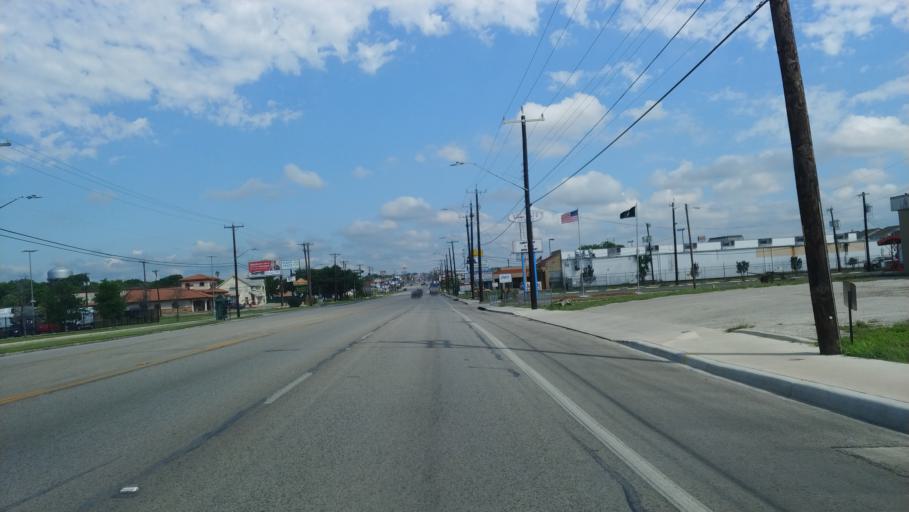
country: US
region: Texas
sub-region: Bexar County
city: Balcones Heights
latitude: 29.4761
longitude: -98.5375
